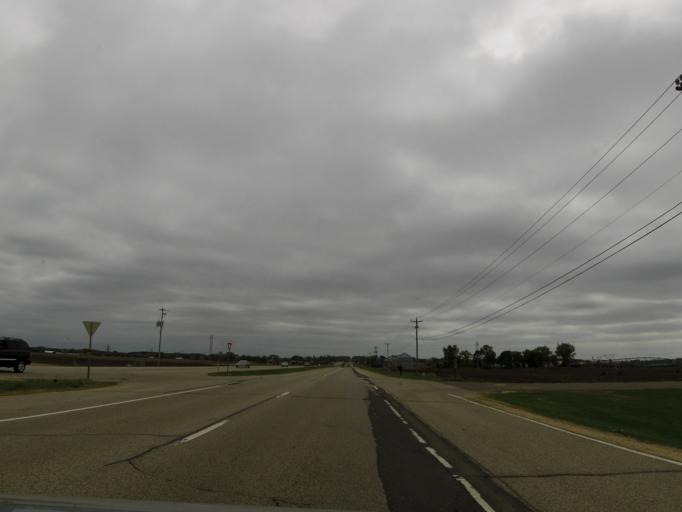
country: US
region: Minnesota
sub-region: Washington County
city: Lake Elmo
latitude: 44.9604
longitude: -92.8629
